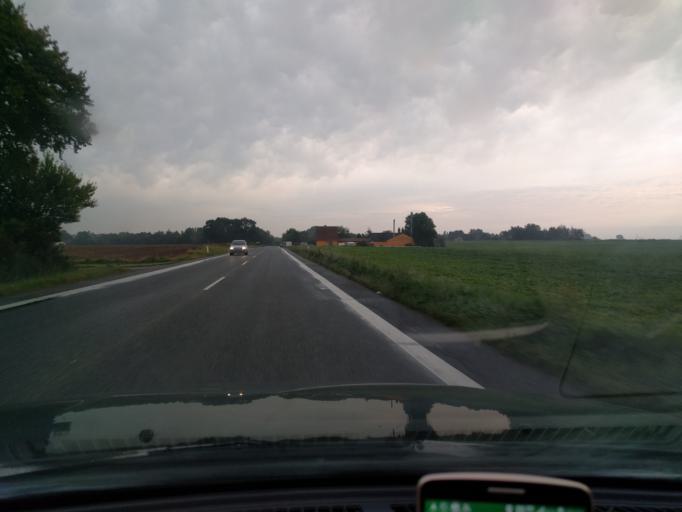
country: DK
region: Zealand
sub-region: Guldborgsund Kommune
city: Norre Alslev
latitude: 54.9058
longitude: 11.8744
